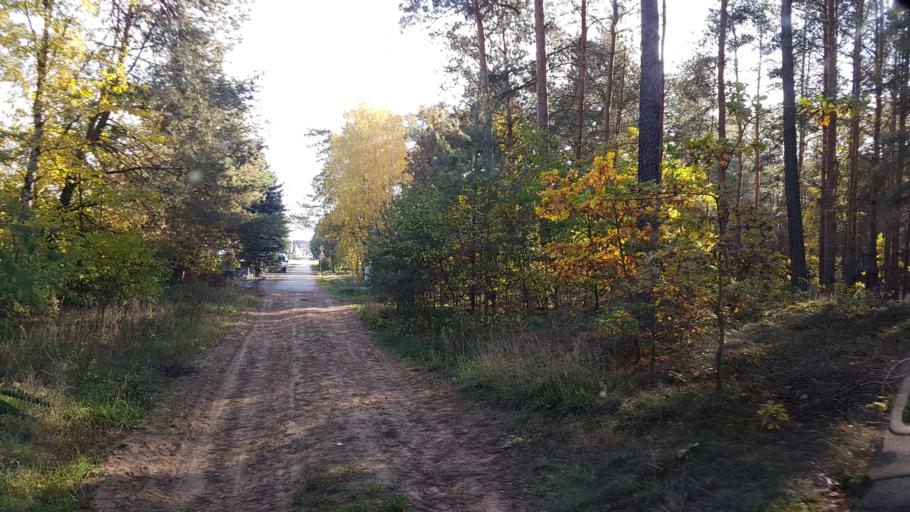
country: DE
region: Brandenburg
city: Hohenbucko
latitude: 51.6936
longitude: 13.5052
